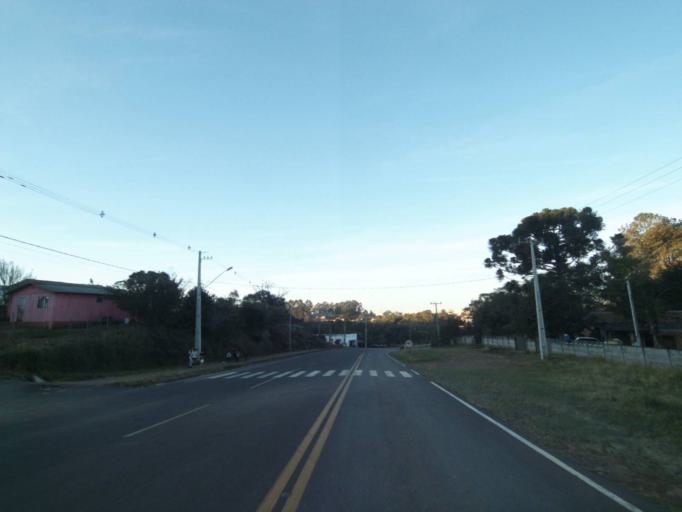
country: BR
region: Parana
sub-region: Tibagi
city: Tibagi
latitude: -24.5126
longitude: -50.4229
